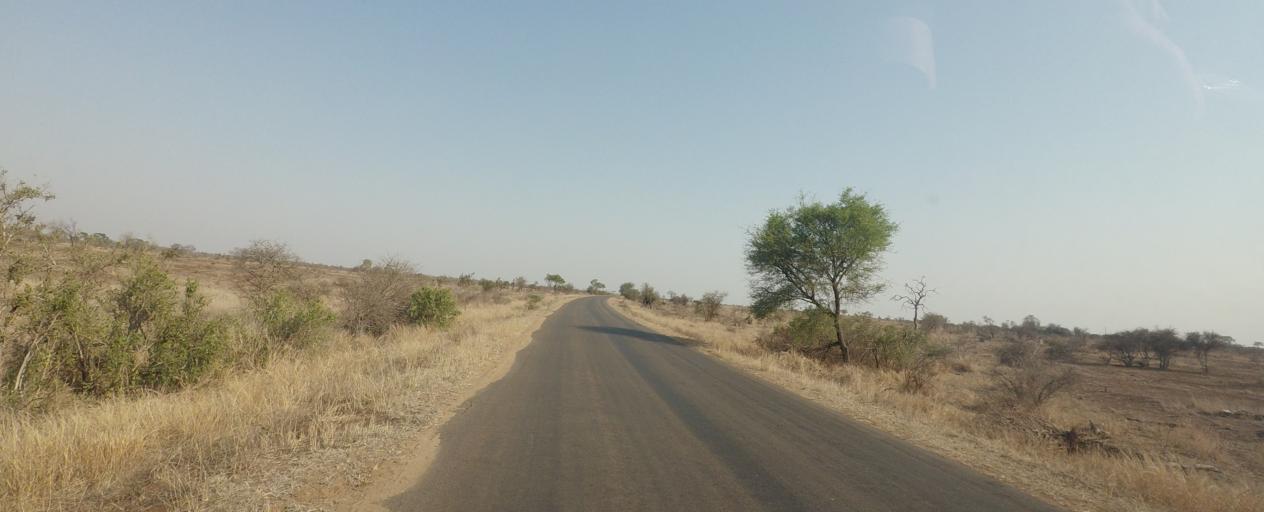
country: ZA
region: Limpopo
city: Thulamahashi
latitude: -24.3873
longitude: 31.7734
